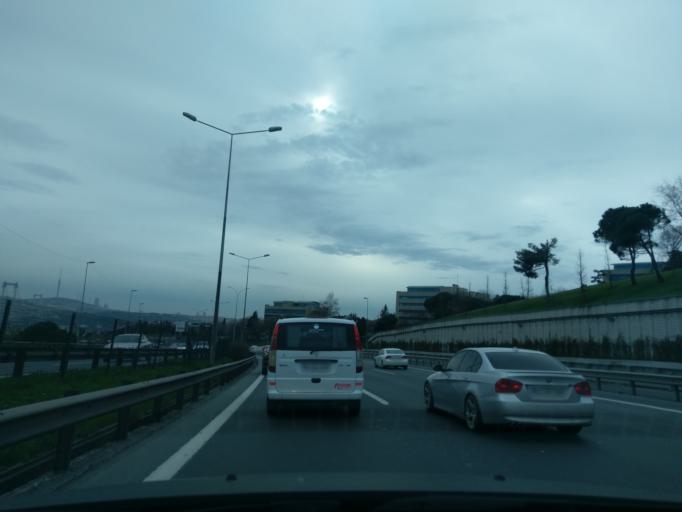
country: TR
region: Istanbul
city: Sisli
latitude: 41.0601
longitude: 29.0158
